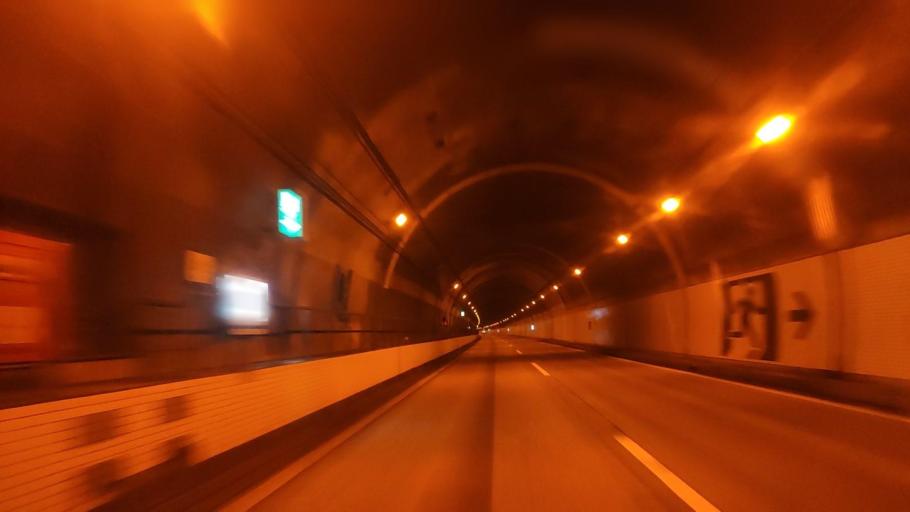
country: JP
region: Toyama
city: Nyuzen
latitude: 36.9774
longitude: 137.6570
